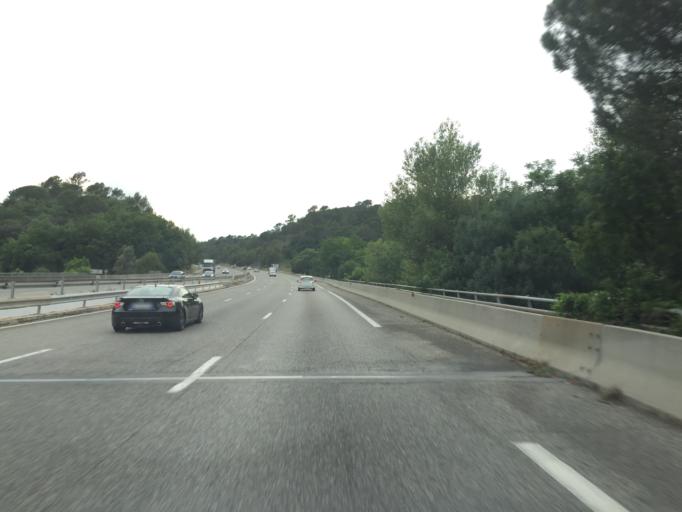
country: FR
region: Provence-Alpes-Cote d'Azur
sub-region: Departement du Var
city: Le Val
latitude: 43.4196
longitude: 6.0982
